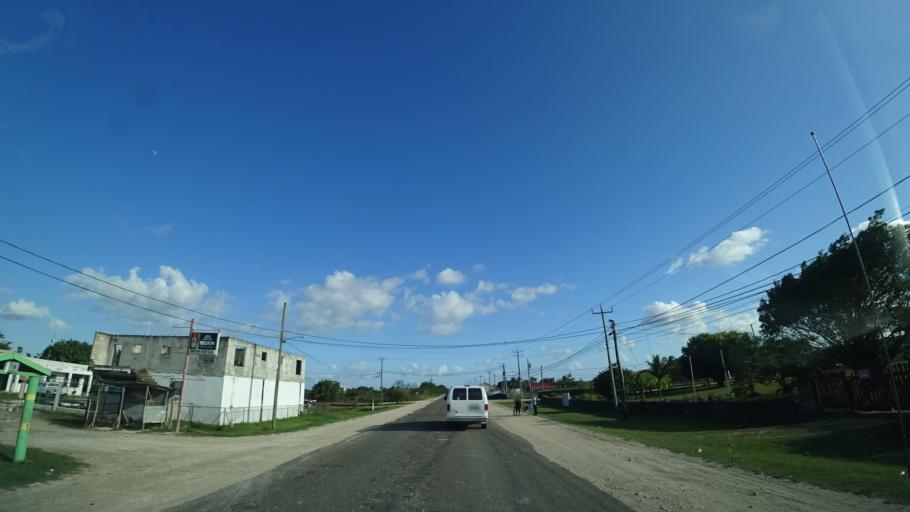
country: BZ
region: Belize
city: Belize City
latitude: 17.5641
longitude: -88.3254
